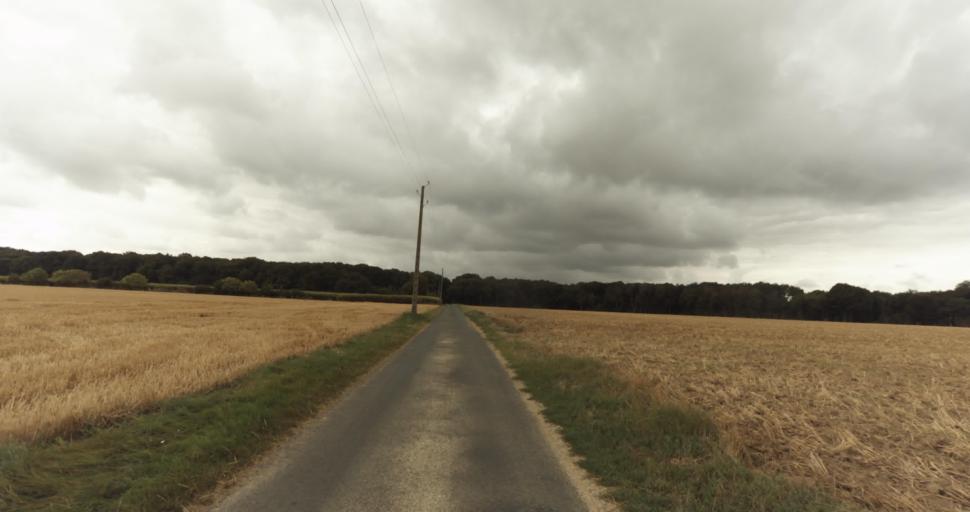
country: FR
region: Haute-Normandie
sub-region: Departement de l'Eure
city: Menilles
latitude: 49.0118
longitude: 1.2706
